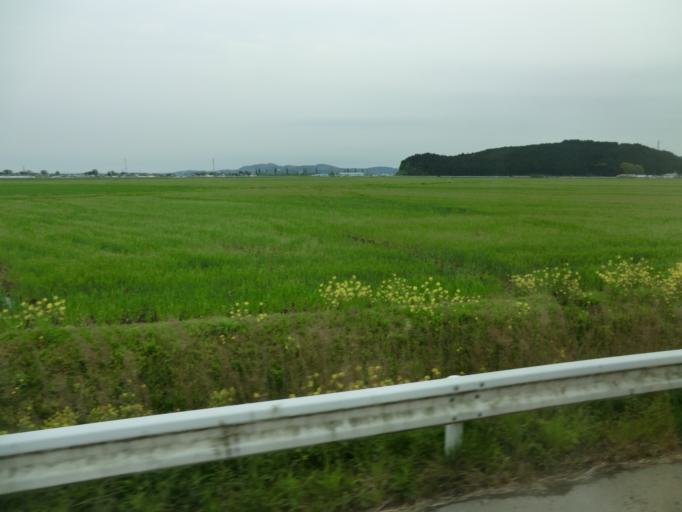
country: JP
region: Miyagi
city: Yamoto
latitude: 38.5309
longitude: 141.2450
